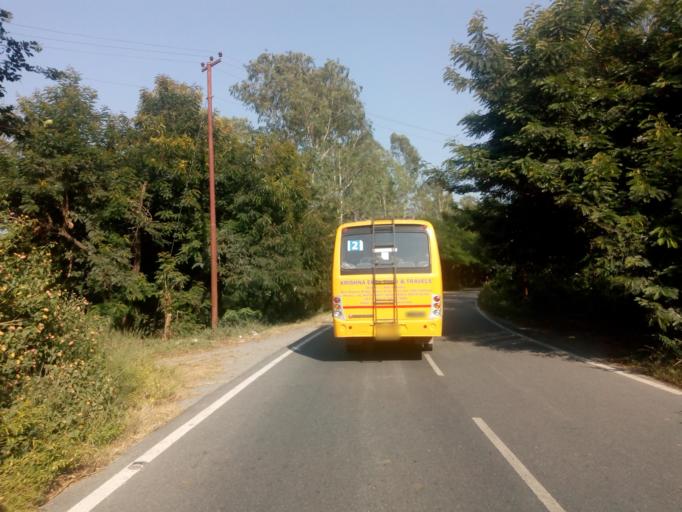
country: IN
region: Uttarakhand
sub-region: Dehradun
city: Harbatpur
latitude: 30.4430
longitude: 77.7019
